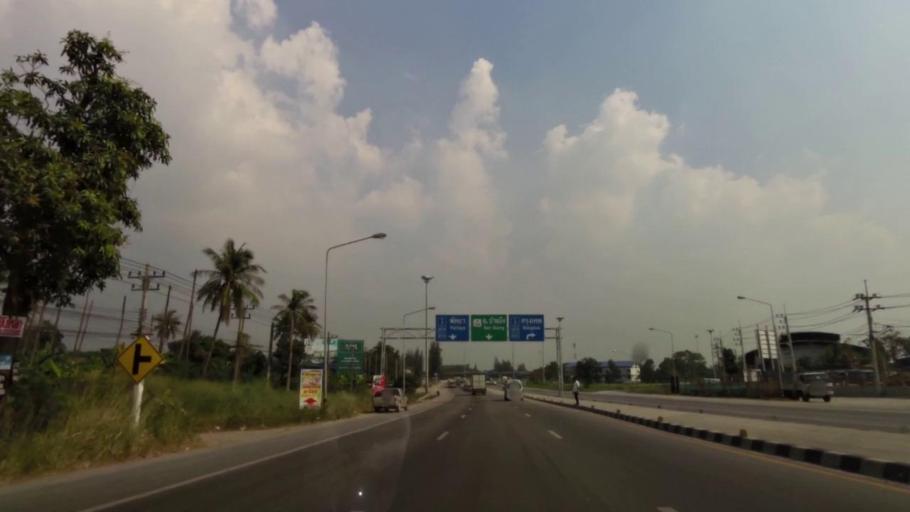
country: TH
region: Chon Buri
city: Chon Buri
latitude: 13.3470
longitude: 101.0242
